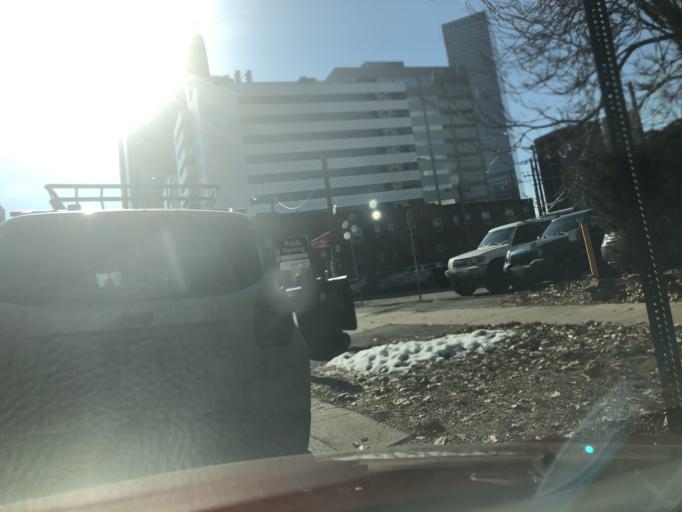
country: US
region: Colorado
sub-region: Denver County
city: Denver
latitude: 39.7470
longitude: -104.9847
